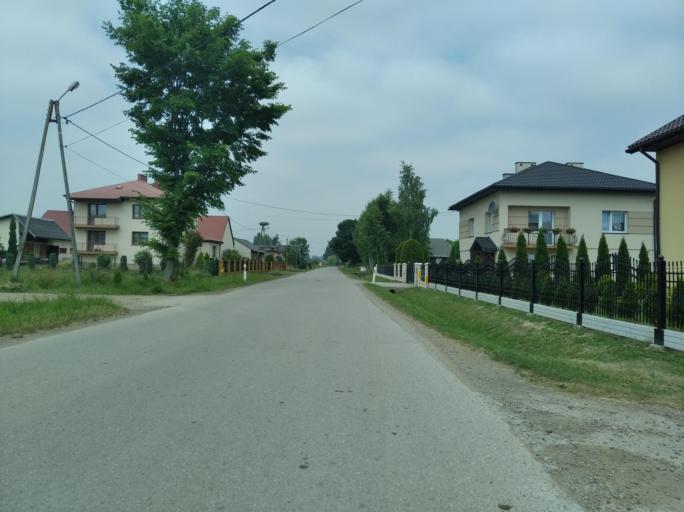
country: PL
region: Subcarpathian Voivodeship
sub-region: Powiat sanocki
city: Besko
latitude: 49.6173
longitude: 21.9446
